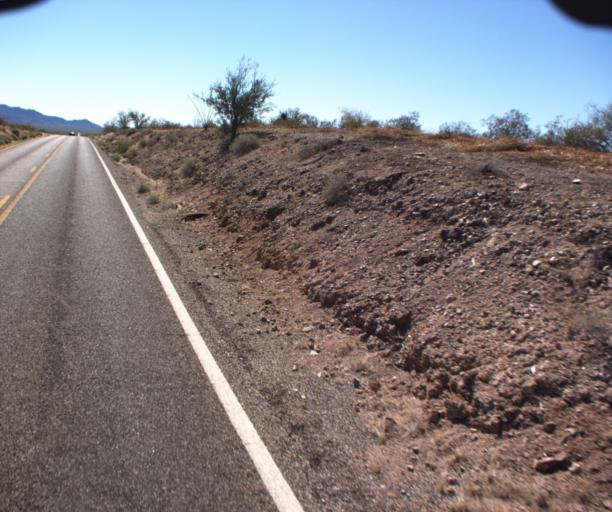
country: US
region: Arizona
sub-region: Pima County
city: Ajo
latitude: 32.3499
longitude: -112.8167
